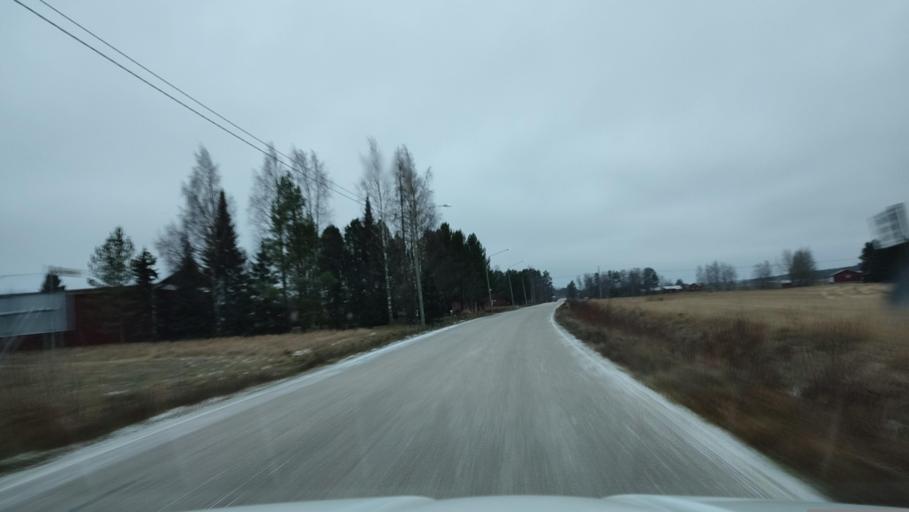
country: FI
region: Southern Ostrobothnia
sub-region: Suupohja
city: Karijoki
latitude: 62.2592
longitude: 21.6802
